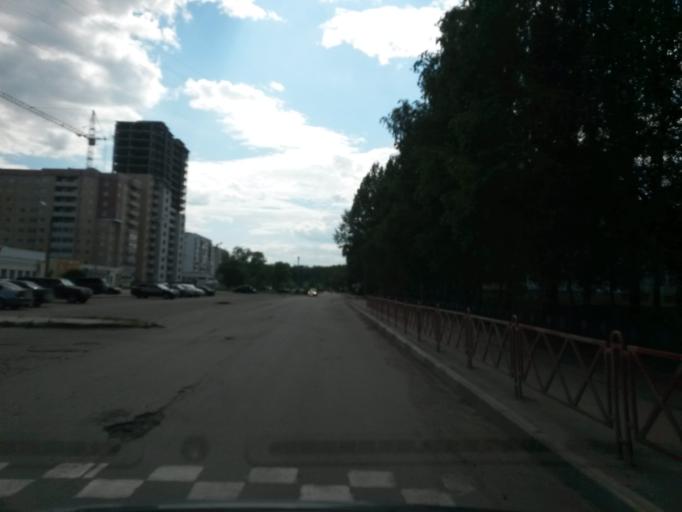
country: RU
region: Jaroslavl
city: Yaroslavl
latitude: 57.6455
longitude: 39.9502
